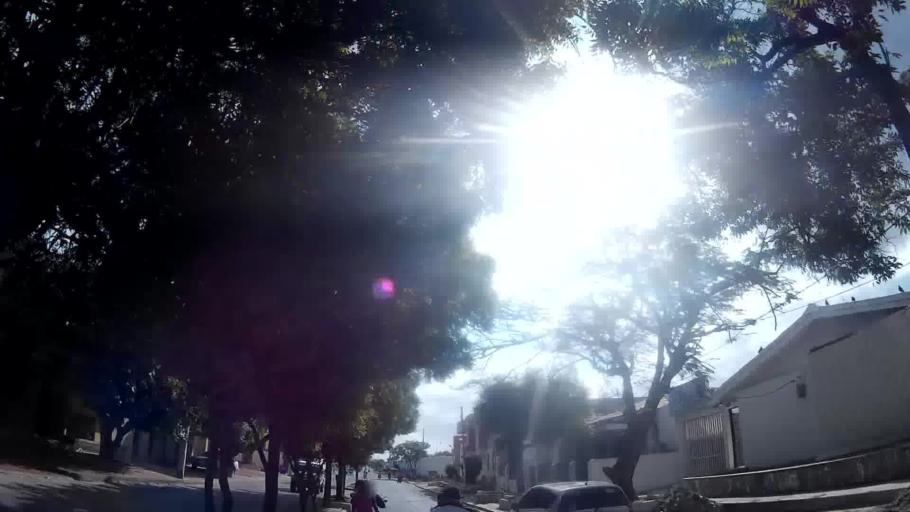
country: CO
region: La Guajira
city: Maicao
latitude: 11.3817
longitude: -72.2387
